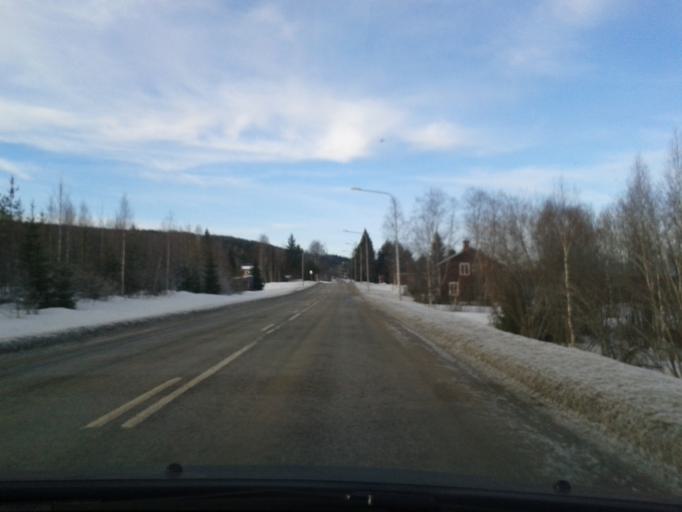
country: SE
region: Vaesternorrland
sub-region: OErnskoeldsviks Kommun
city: Bredbyn
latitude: 63.4834
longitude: 18.0886
